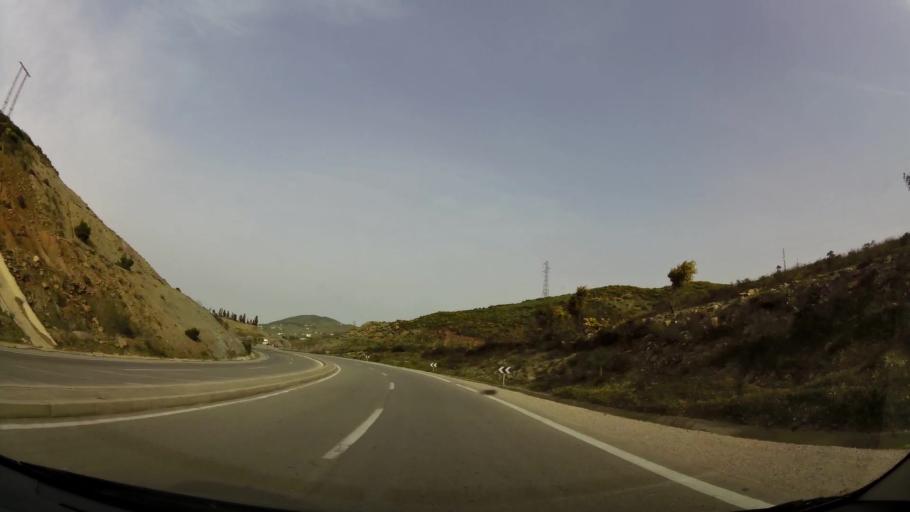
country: MA
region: Tanger-Tetouan
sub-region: Tetouan
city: Saddina
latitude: 35.5483
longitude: -5.5311
